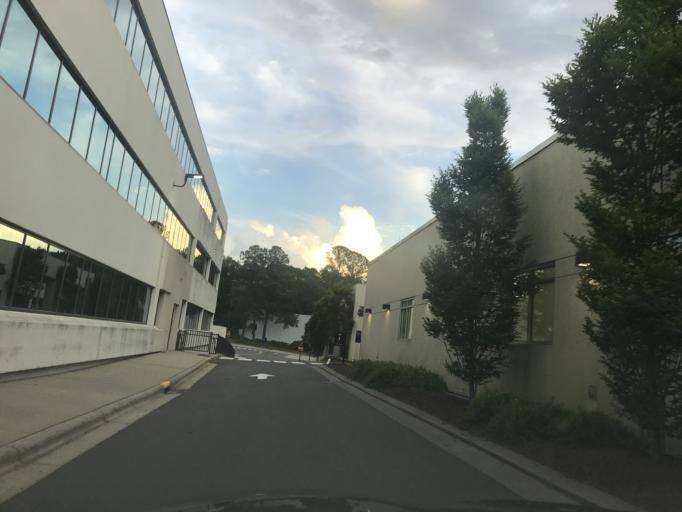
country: US
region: North Carolina
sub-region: Wake County
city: Raleigh
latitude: 35.8287
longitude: -78.6180
